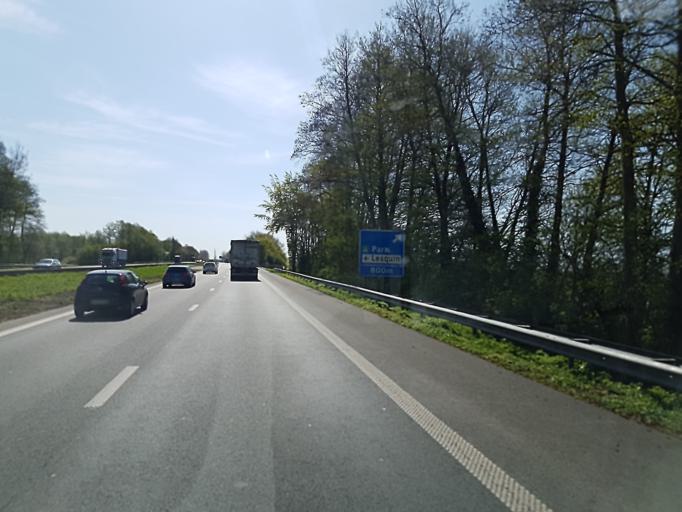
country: FR
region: Nord-Pas-de-Calais
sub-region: Departement du Nord
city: Camphin-en-Pevele
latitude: 50.6257
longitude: 3.3142
